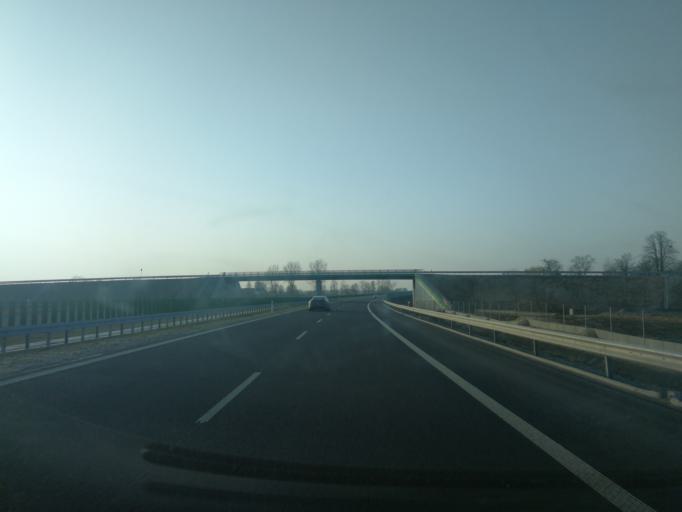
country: PL
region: Pomeranian Voivodeship
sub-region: Powiat nowodworski
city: Nowy Dwor Gdanski
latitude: 54.1755
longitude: 19.1913
